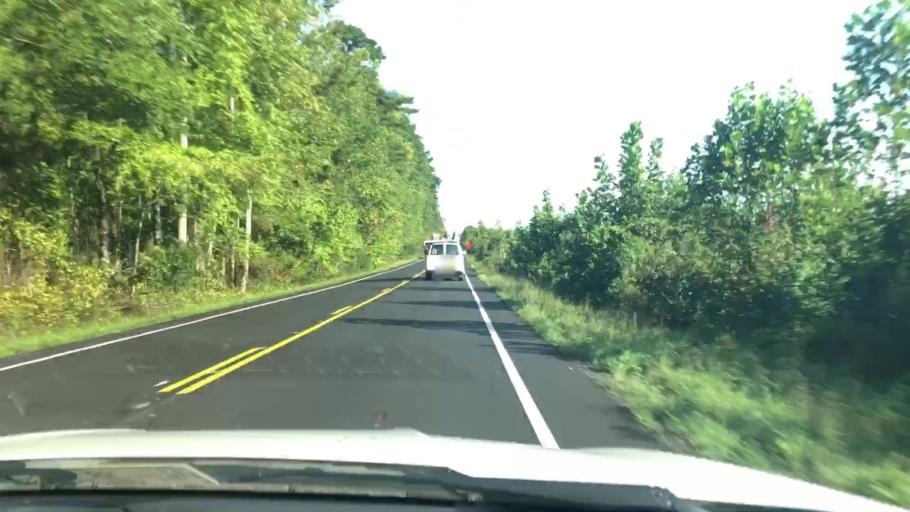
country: US
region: Virginia
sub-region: King William County
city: West Point
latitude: 37.4723
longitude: -76.8451
